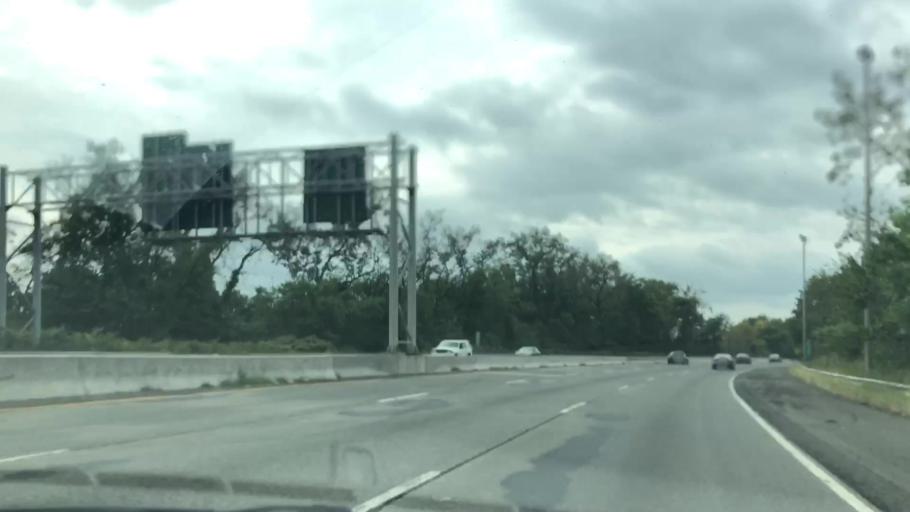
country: US
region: New Jersey
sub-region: Bergen County
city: Lyndhurst
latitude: 40.8216
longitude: -74.1275
